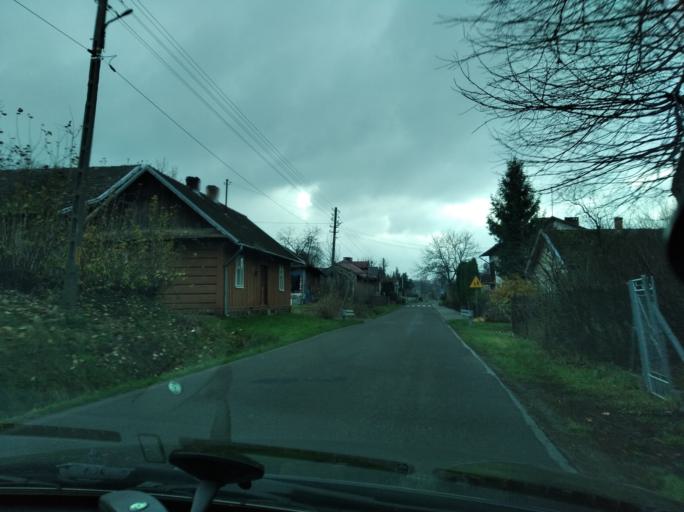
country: PL
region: Subcarpathian Voivodeship
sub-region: Powiat przeworski
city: Sietesz
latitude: 49.9915
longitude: 22.3526
